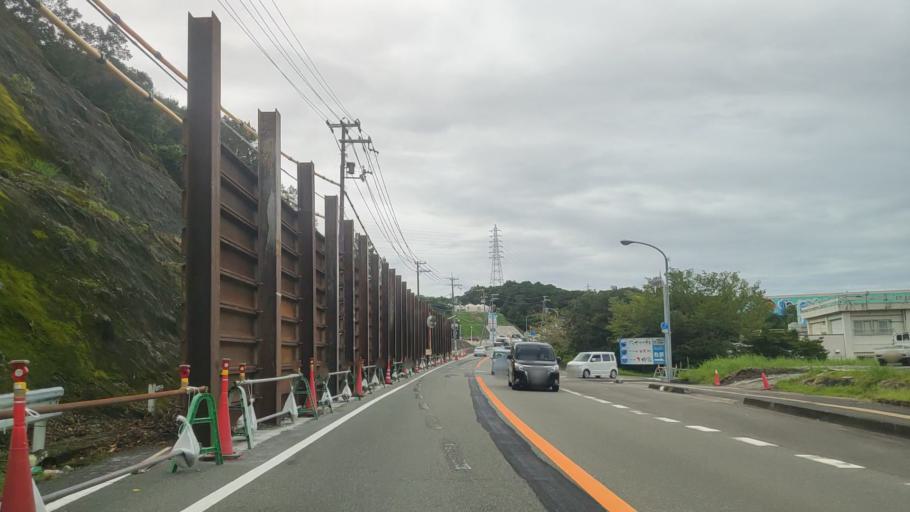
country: JP
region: Wakayama
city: Tanabe
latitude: 33.6825
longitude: 135.3780
